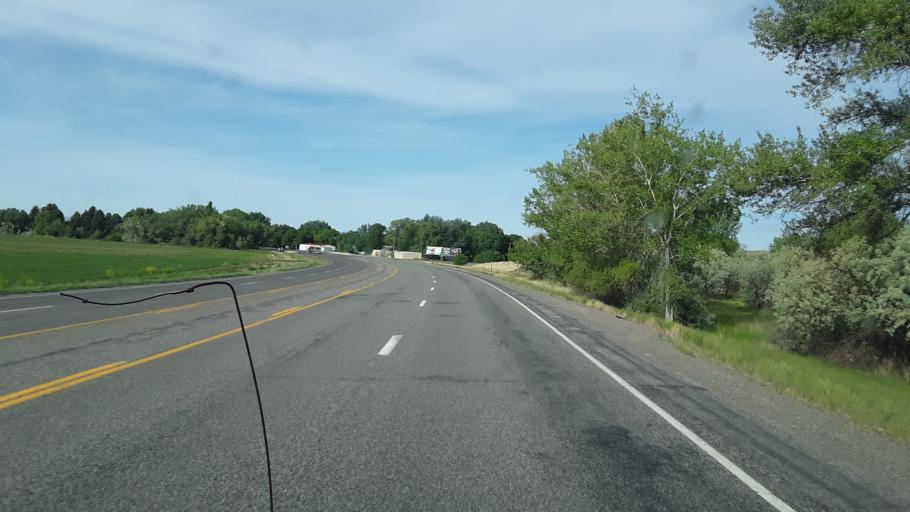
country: US
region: Wyoming
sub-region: Fremont County
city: Riverton
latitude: 43.0842
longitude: -108.3774
